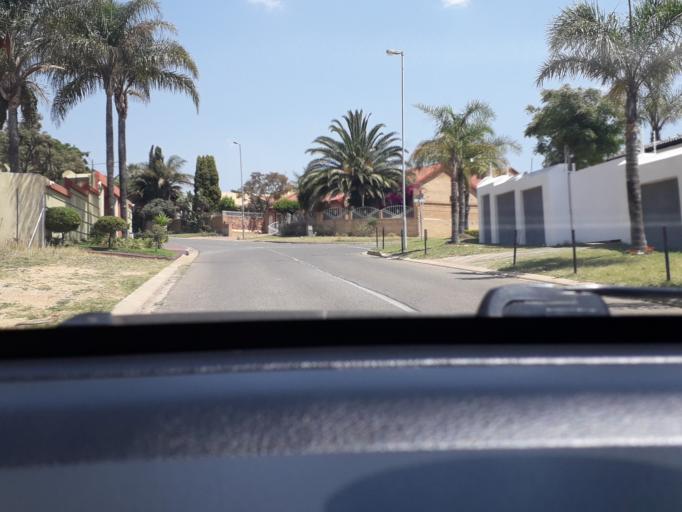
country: ZA
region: Gauteng
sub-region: City of Johannesburg Metropolitan Municipality
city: Modderfontein
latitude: -26.0912
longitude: 28.0925
